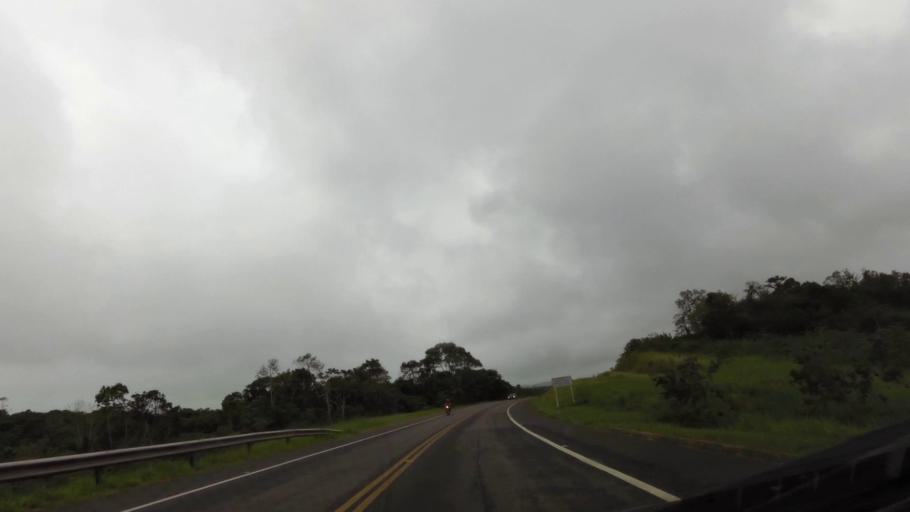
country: BR
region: Espirito Santo
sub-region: Guarapari
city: Guarapari
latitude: -20.7189
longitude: -40.5751
